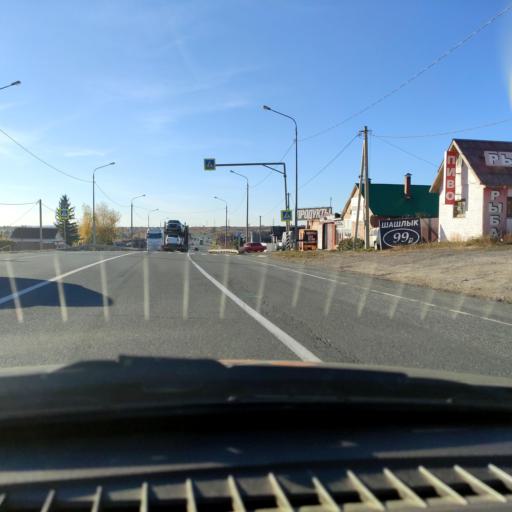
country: RU
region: Samara
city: Mezhdurechensk
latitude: 53.2479
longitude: 49.1824
